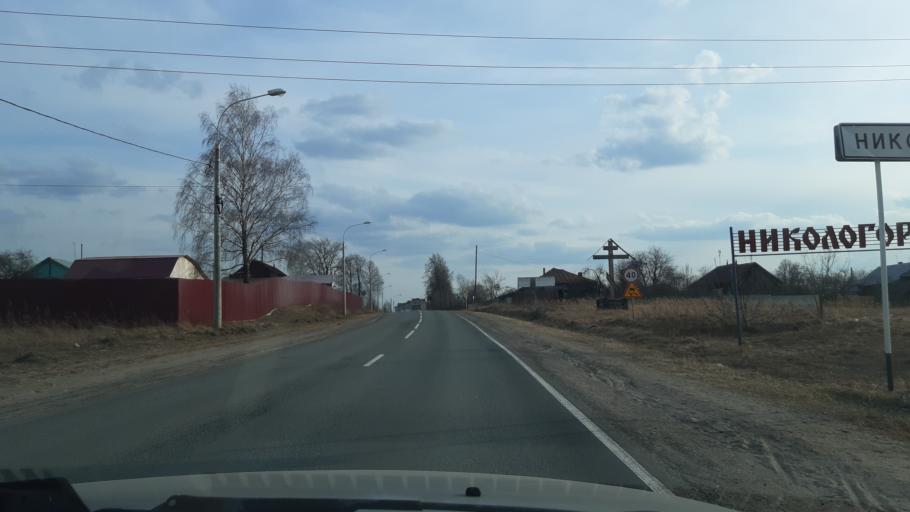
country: RU
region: Vladimir
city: Nikologory
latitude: 56.1524
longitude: 41.9956
